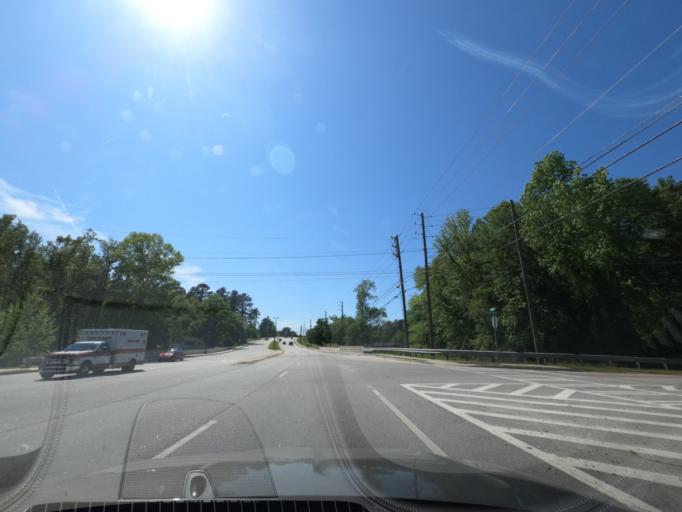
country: US
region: Georgia
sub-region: Columbia County
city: Martinez
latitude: 33.4705
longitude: -82.1059
